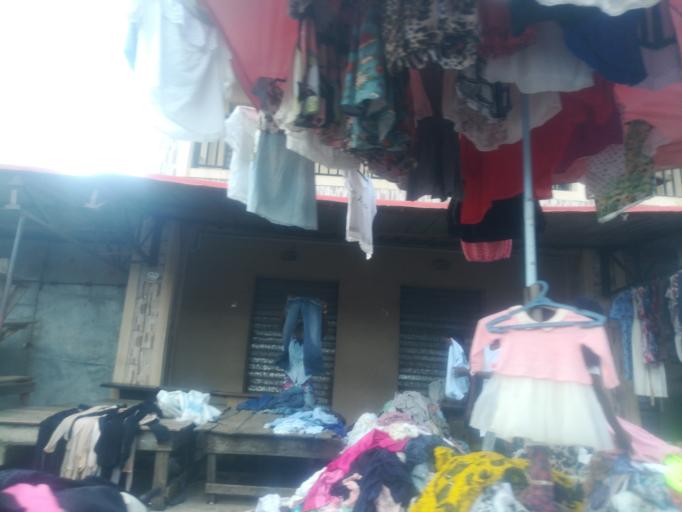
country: NG
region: Oyo
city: Ibadan
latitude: 7.3887
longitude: 3.8832
